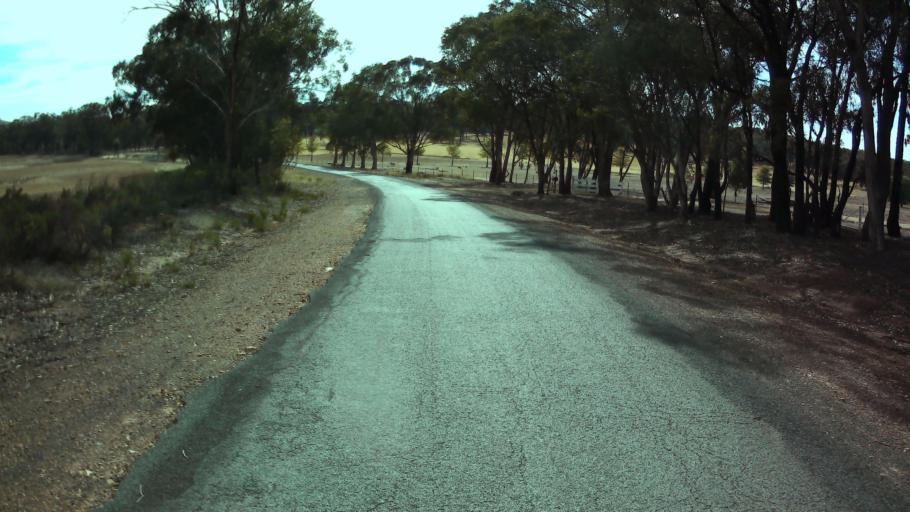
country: AU
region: New South Wales
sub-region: Weddin
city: Grenfell
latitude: -33.8493
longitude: 148.2305
